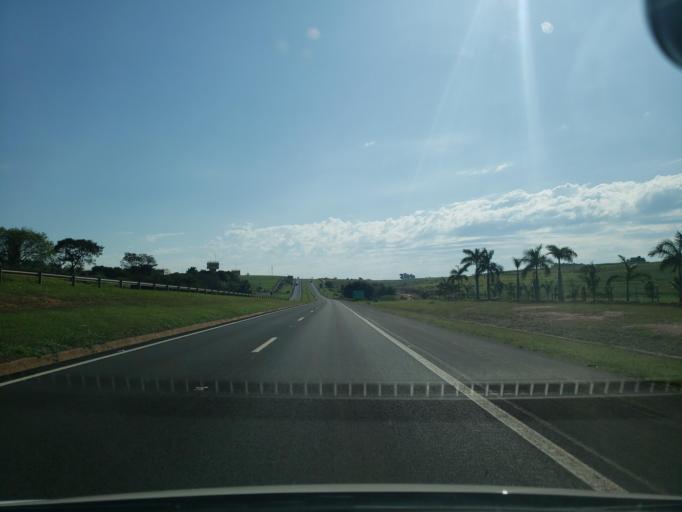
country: BR
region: Sao Paulo
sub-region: Penapolis
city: Penapolis
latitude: -21.5194
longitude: -50.0020
